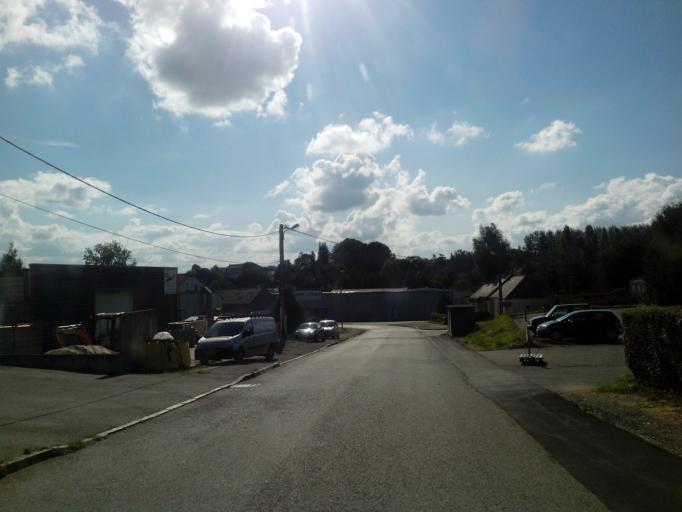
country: FR
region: Brittany
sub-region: Departement des Cotes-d'Armor
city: Merdrignac
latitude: 48.1917
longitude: -2.4017
